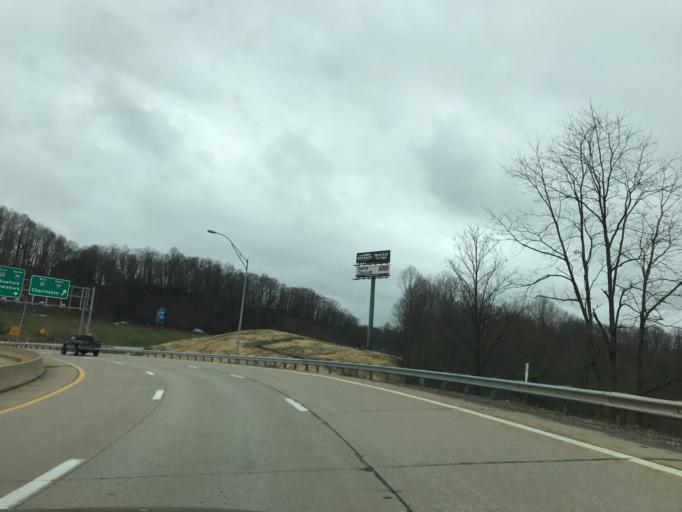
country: US
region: West Virginia
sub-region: Raleigh County
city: MacArthur
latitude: 37.7629
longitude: -81.2124
